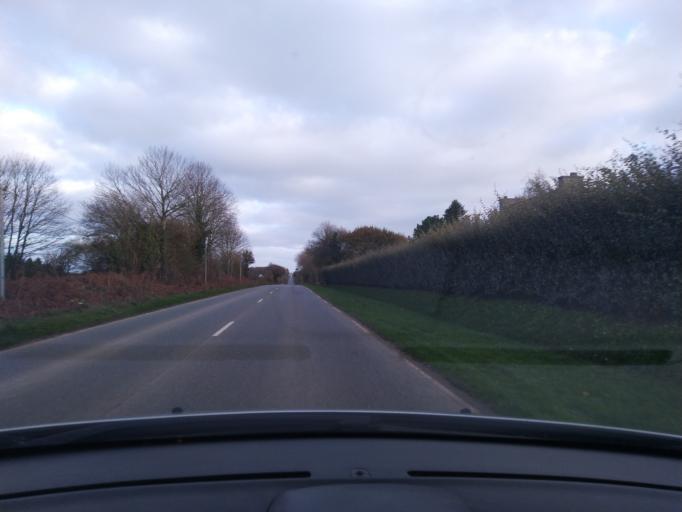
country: FR
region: Brittany
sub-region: Departement du Finistere
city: Plourin-les-Morlaix
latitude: 48.5743
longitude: -3.7517
